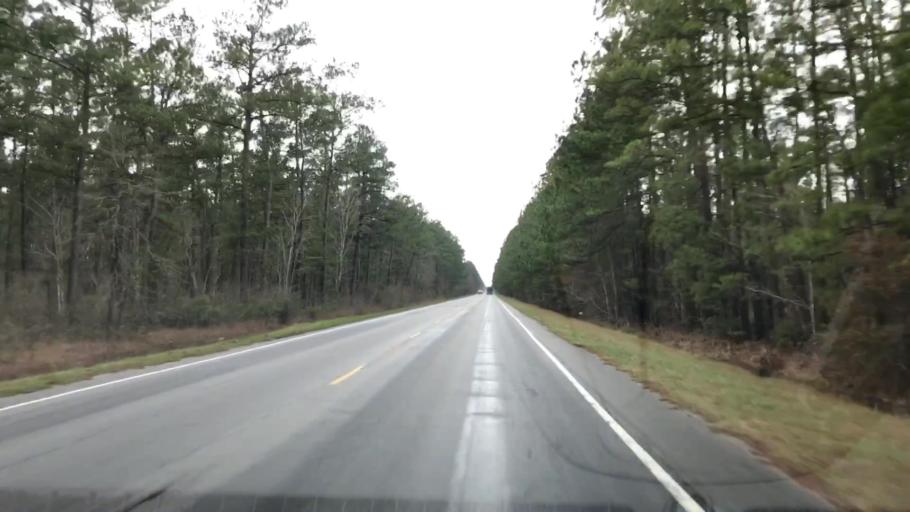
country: US
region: South Carolina
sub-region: Berkeley County
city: Saint Stephen
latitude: 33.2877
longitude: -79.8343
